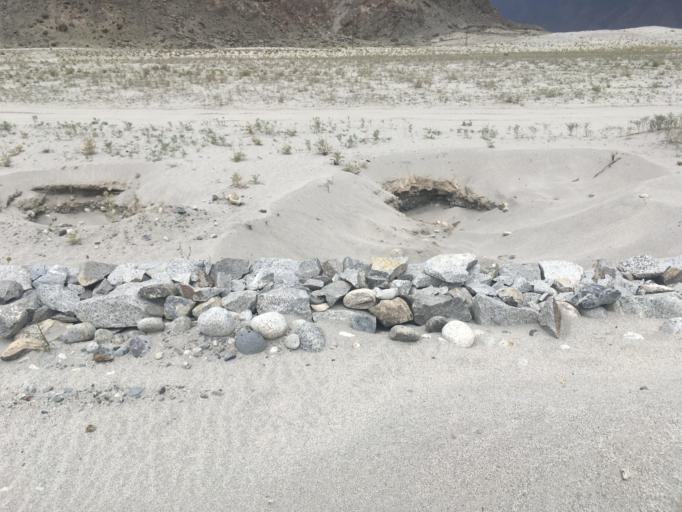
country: PK
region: Gilgit-Baltistan
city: Skardu
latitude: 35.3154
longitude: 75.6575
